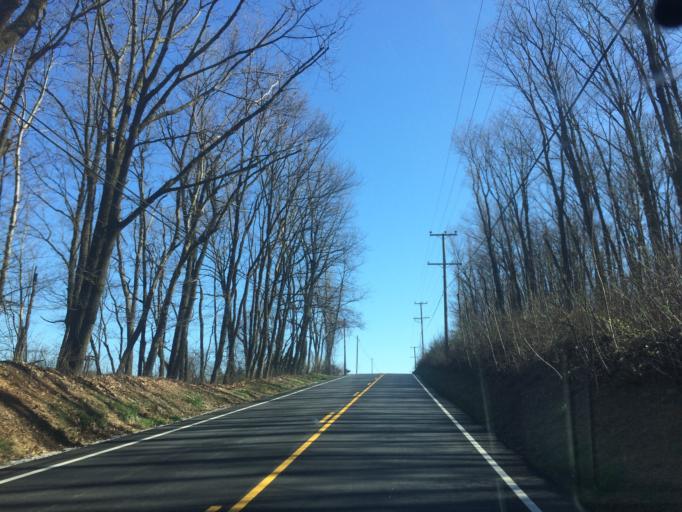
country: US
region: Maryland
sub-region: Carroll County
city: Westminster
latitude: 39.6417
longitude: -76.9802
